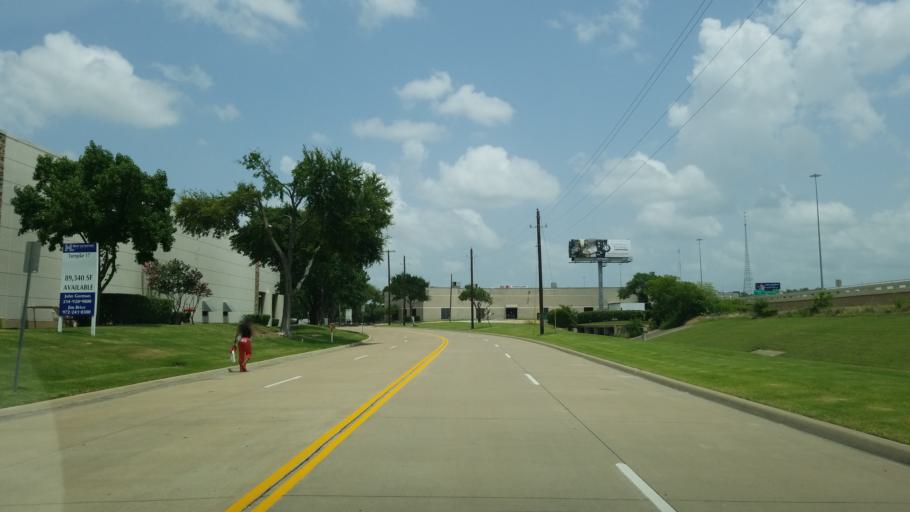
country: US
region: Texas
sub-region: Dallas County
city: Cockrell Hill
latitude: 32.7687
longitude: -96.8859
